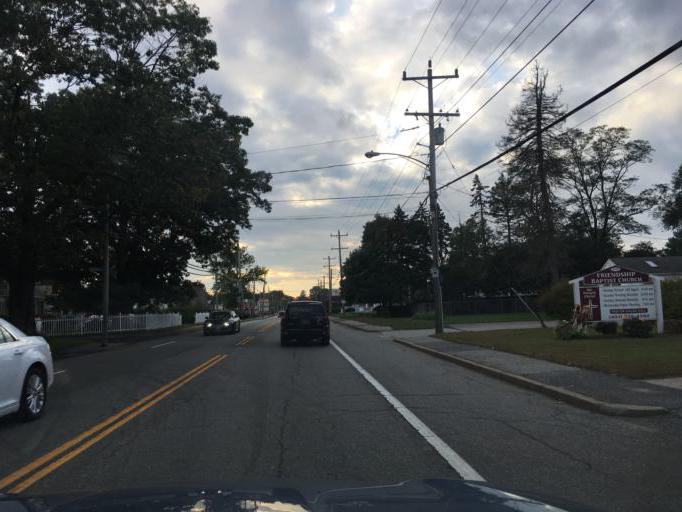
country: US
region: Rhode Island
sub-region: Kent County
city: Warwick
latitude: 41.7027
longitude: -71.4279
